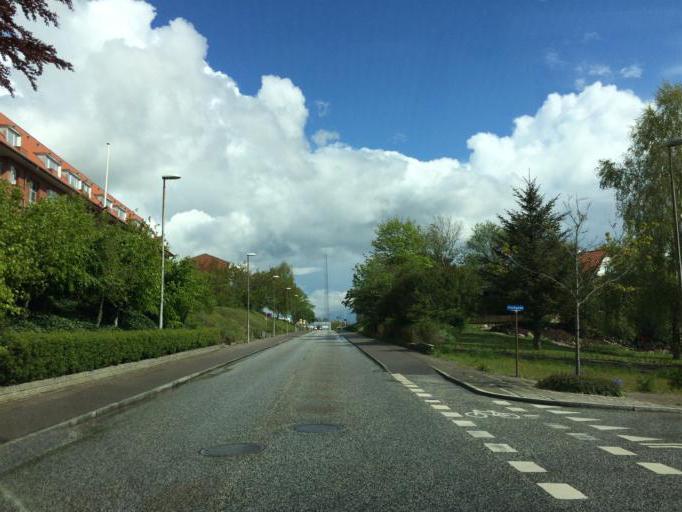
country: DK
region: Central Jutland
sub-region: Holstebro Kommune
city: Holstebro
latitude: 56.3579
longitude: 8.6091
